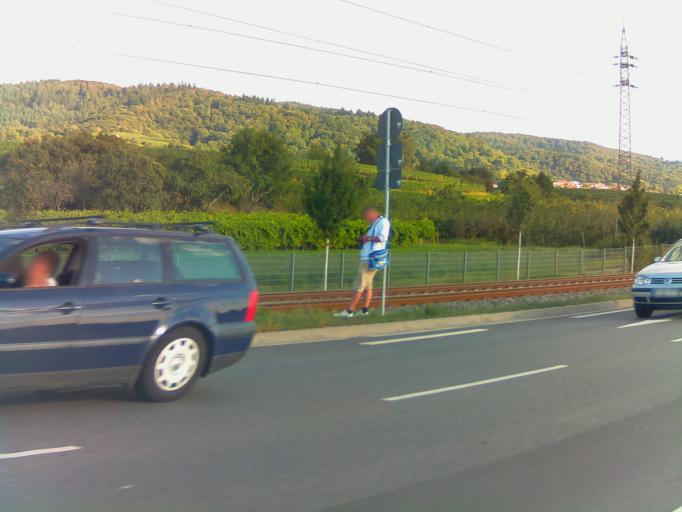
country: DE
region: Baden-Wuerttemberg
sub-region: Karlsruhe Region
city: Schriesheim
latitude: 49.5082
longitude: 8.6559
